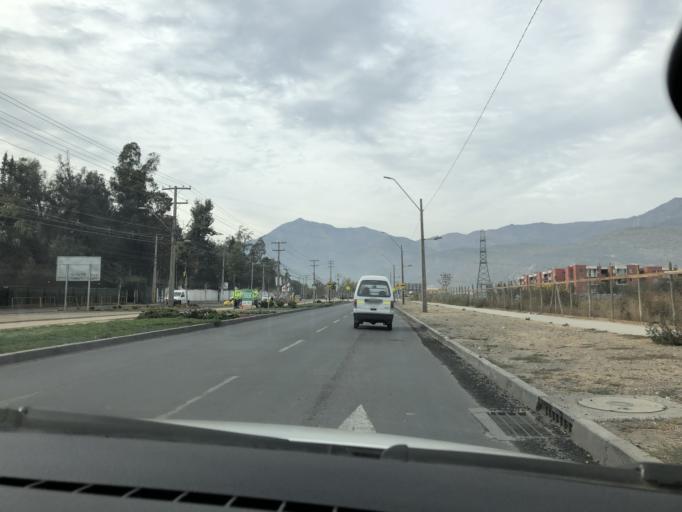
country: CL
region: Santiago Metropolitan
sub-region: Provincia de Cordillera
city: Puente Alto
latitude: -33.6104
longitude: -70.5490
